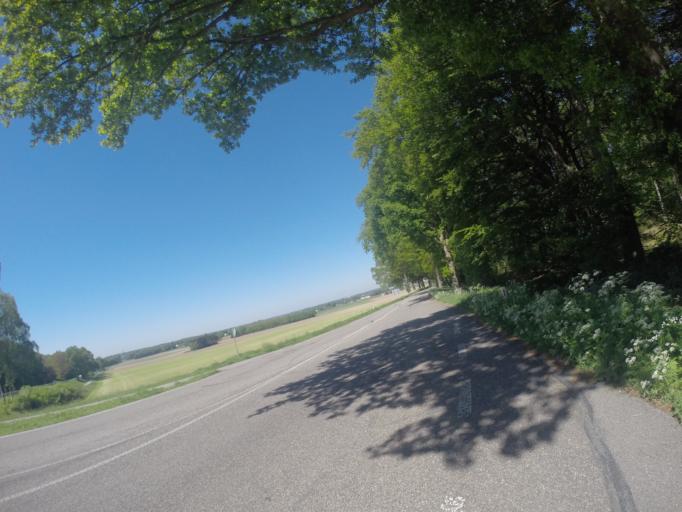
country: NL
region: Gelderland
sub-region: Gemeente Montferland
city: s-Heerenberg
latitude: 51.9111
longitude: 6.2110
